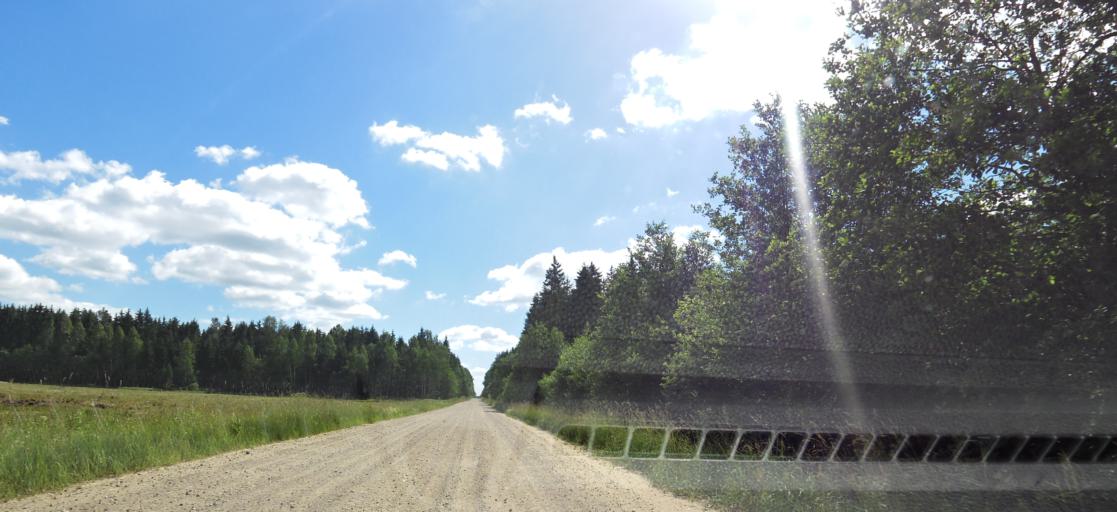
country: LT
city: Vabalninkas
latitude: 56.0042
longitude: 24.8447
